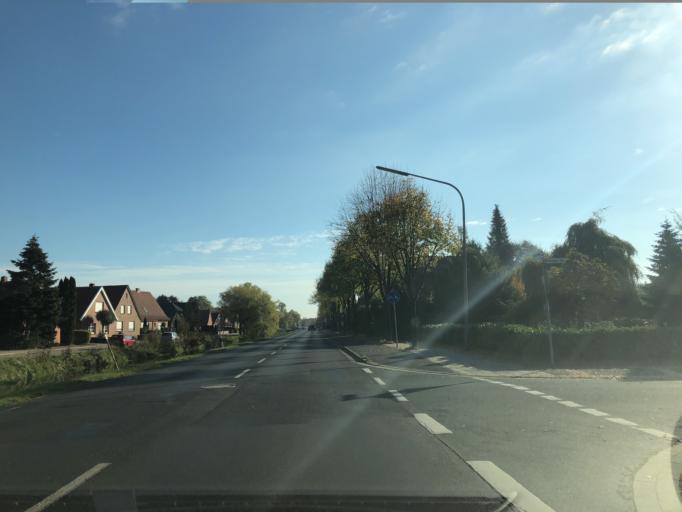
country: DE
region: Lower Saxony
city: Papenburg
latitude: 53.0809
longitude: 7.4239
